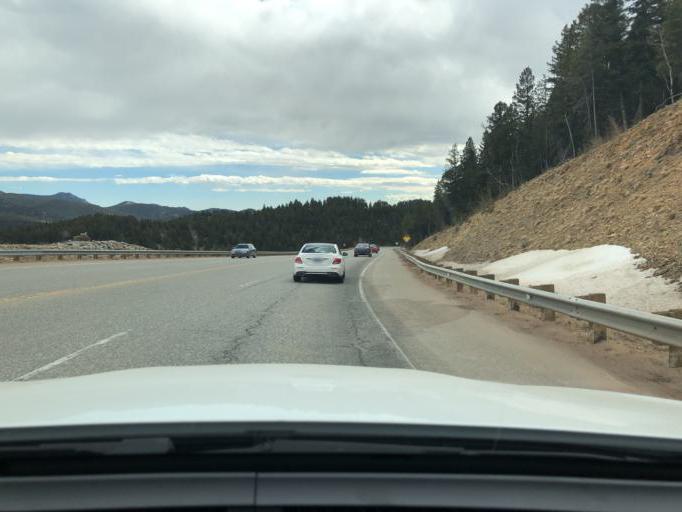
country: US
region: Colorado
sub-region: Gilpin County
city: Central City
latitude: 39.7862
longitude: -105.4870
